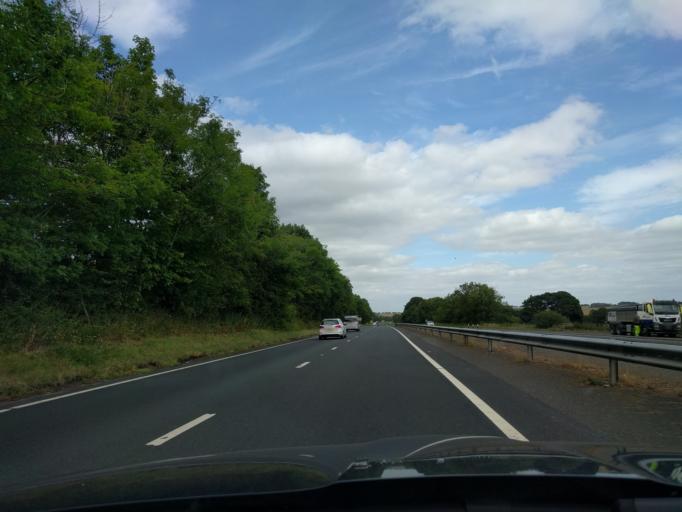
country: GB
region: England
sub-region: Northumberland
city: Felton
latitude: 55.3339
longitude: -1.7254
